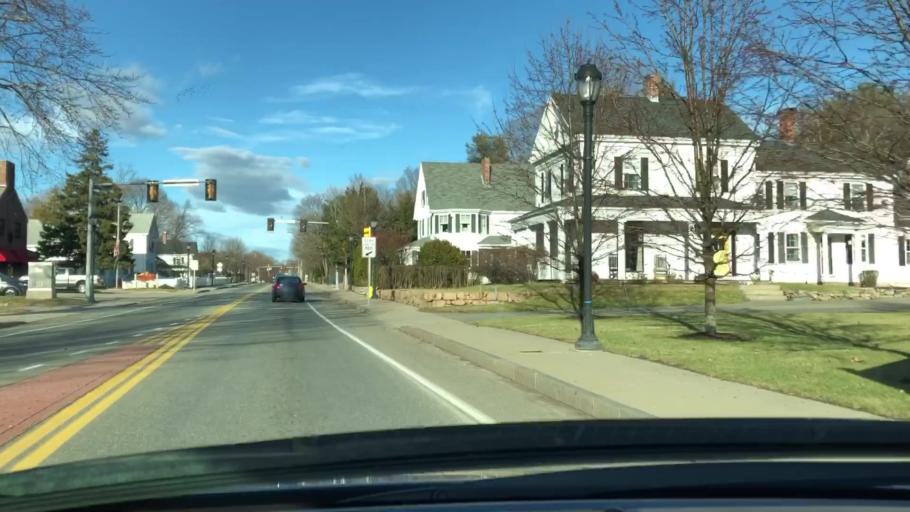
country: US
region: Massachusetts
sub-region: Norfolk County
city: Westwood
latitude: 42.2261
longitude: -71.2222
